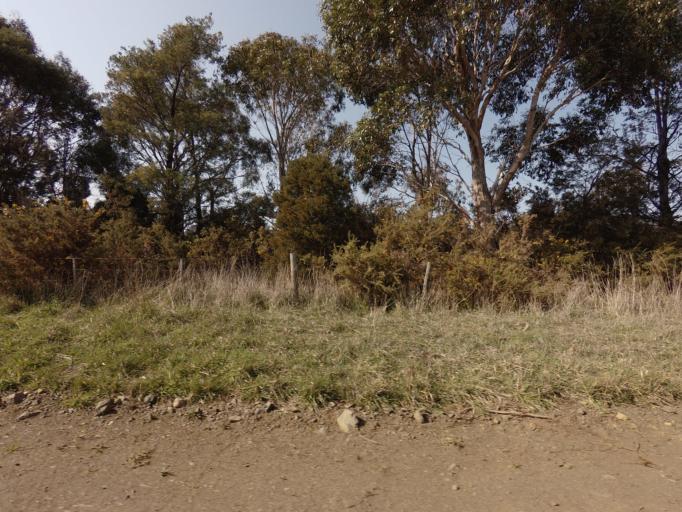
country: AU
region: Tasmania
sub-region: Break O'Day
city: St Helens
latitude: -41.8092
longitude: 147.9424
